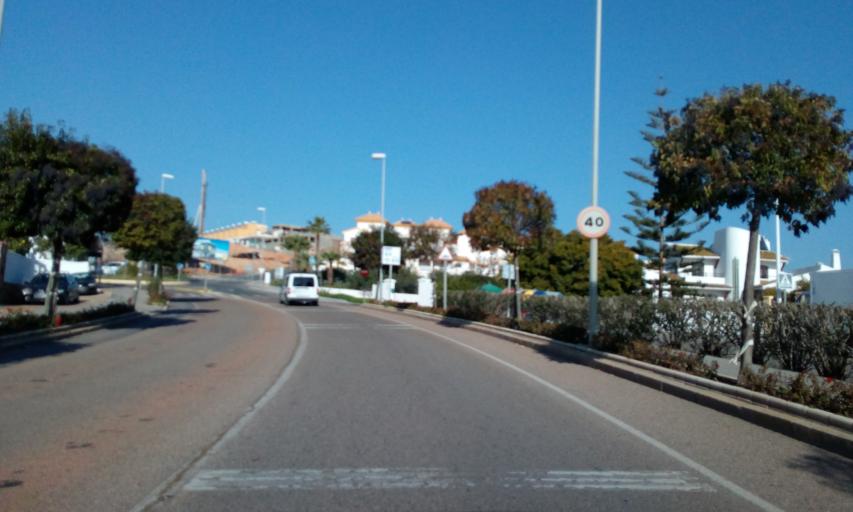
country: ES
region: Andalusia
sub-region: Provincia de Huelva
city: Ayamonte
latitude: 37.2184
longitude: -7.3950
